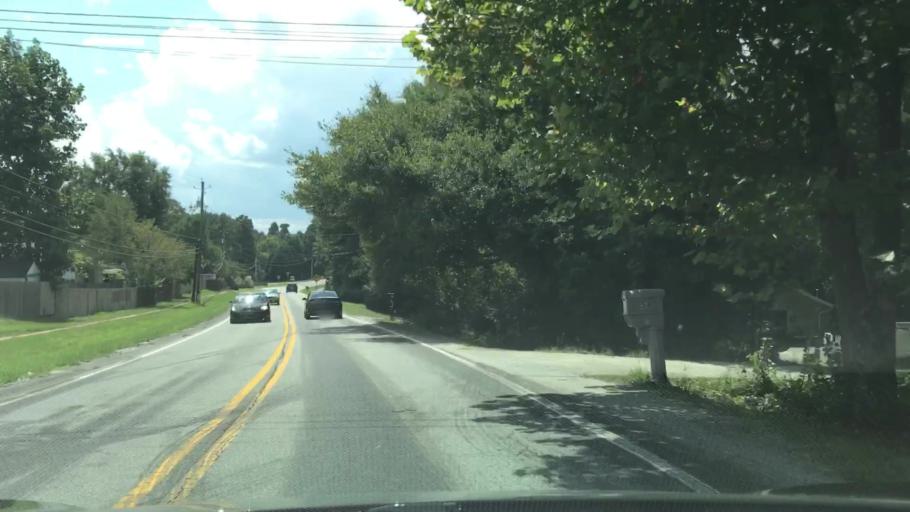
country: US
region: Georgia
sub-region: Gwinnett County
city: Snellville
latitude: 33.9198
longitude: -84.0624
